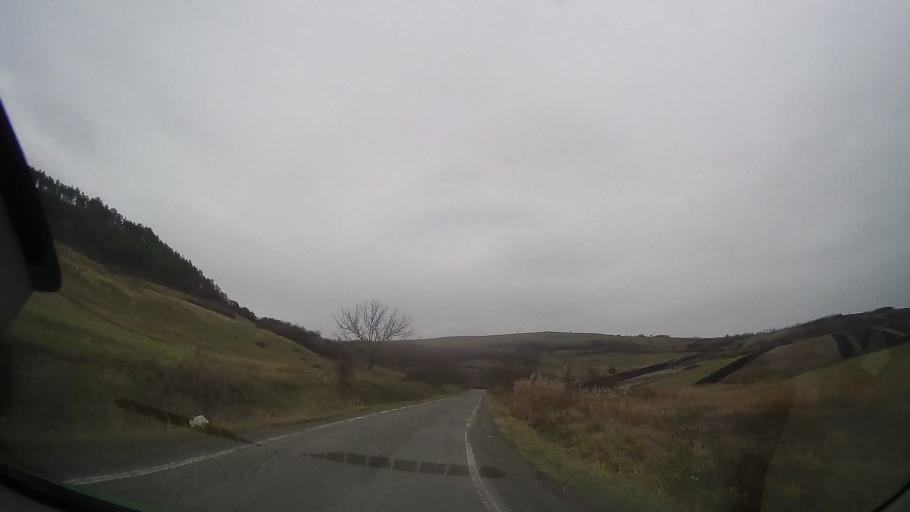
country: RO
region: Mures
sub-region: Comuna Bala
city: Bala
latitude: 46.7158
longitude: 24.5242
